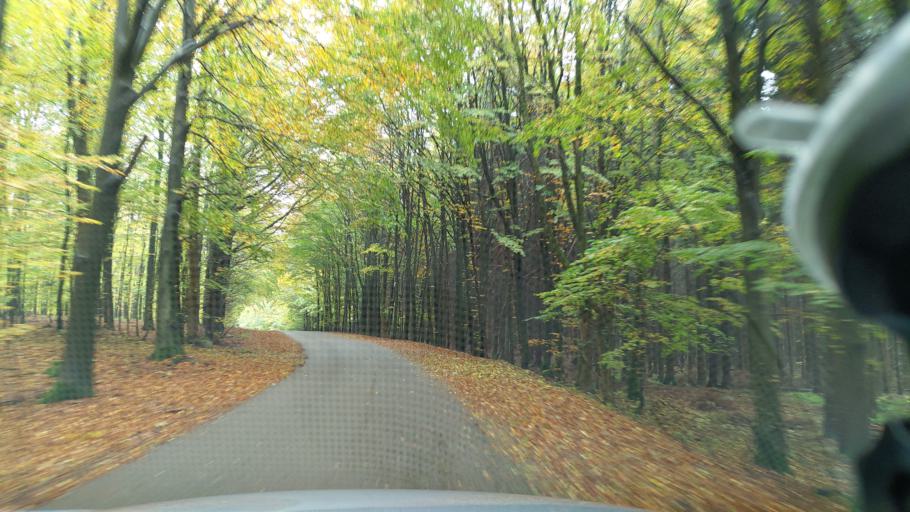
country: DK
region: Zealand
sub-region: Faxe Kommune
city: Ronnede
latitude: 55.2471
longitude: 11.9538
